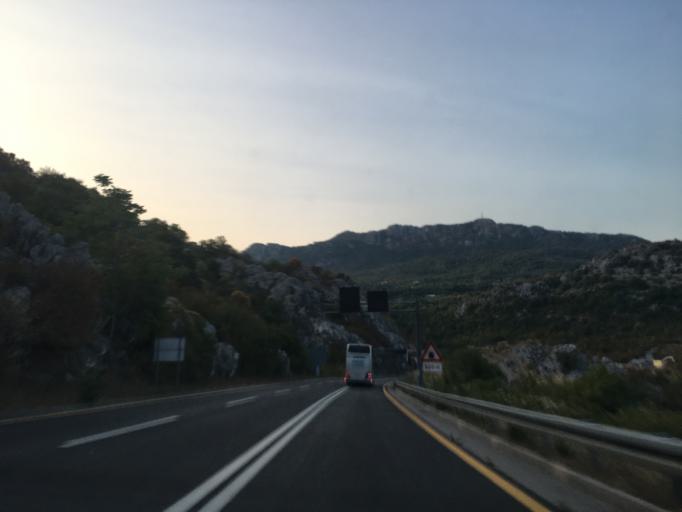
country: ME
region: Bar
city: Sutomore
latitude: 42.2219
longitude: 19.0513
